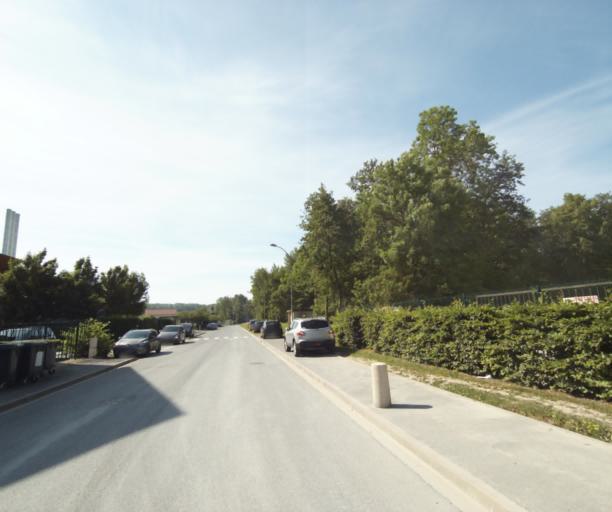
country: FR
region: Champagne-Ardenne
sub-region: Departement des Ardennes
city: Villers-Semeuse
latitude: 49.7410
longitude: 4.7294
